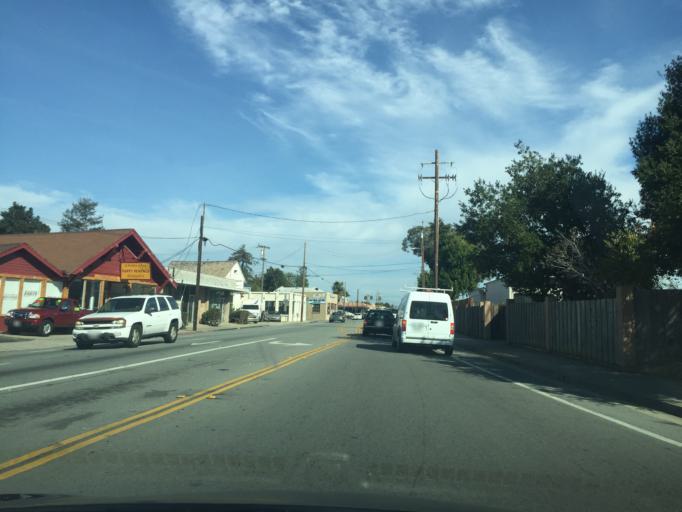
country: US
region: California
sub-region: Santa Cruz County
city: Santa Cruz
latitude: 36.9814
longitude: -122.0140
